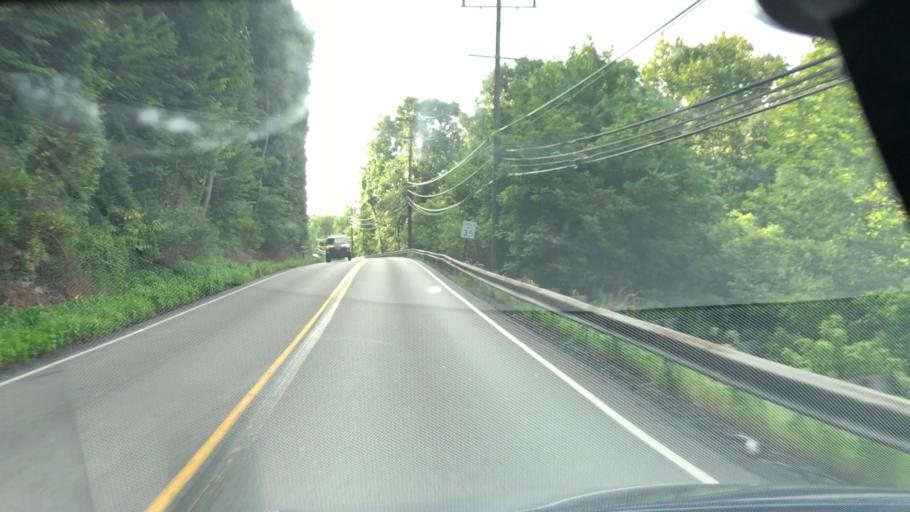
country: US
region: Pennsylvania
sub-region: Washington County
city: Thompsonville
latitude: 40.2889
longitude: -80.1027
